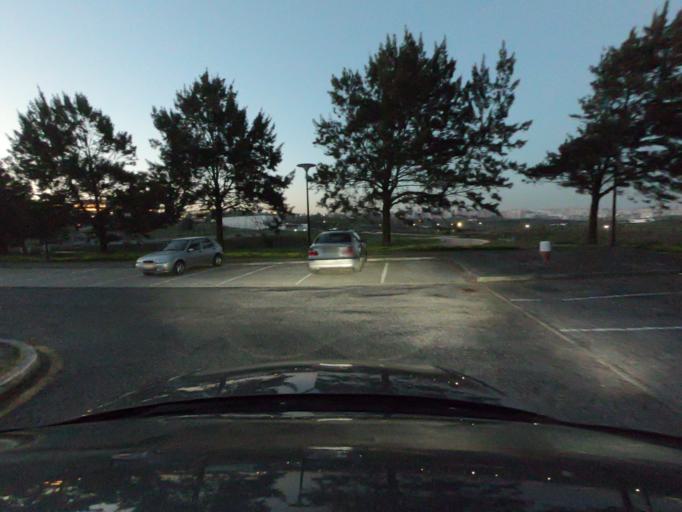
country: PT
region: Lisbon
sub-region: Oeiras
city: Porto Salvo
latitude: 38.7370
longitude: -9.3017
